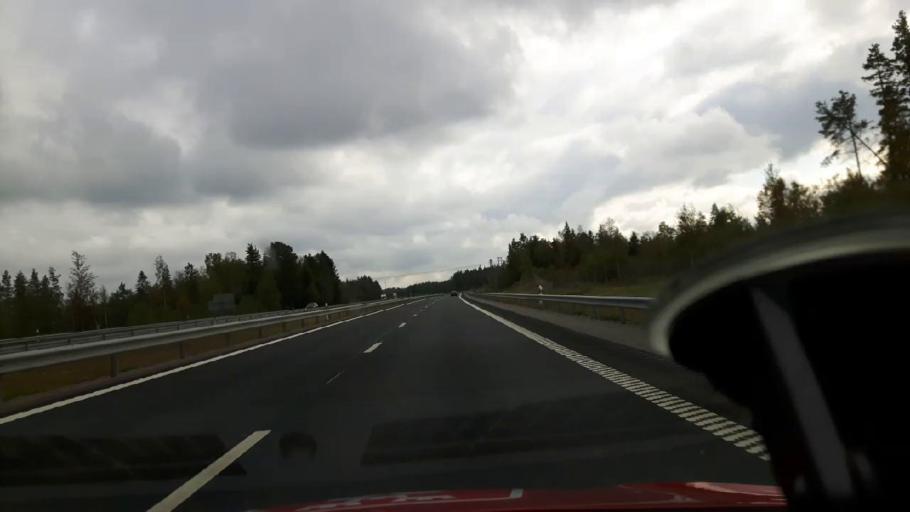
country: SE
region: Gaevleborg
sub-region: Gavle Kommun
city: Gavle
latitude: 60.6291
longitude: 17.1518
